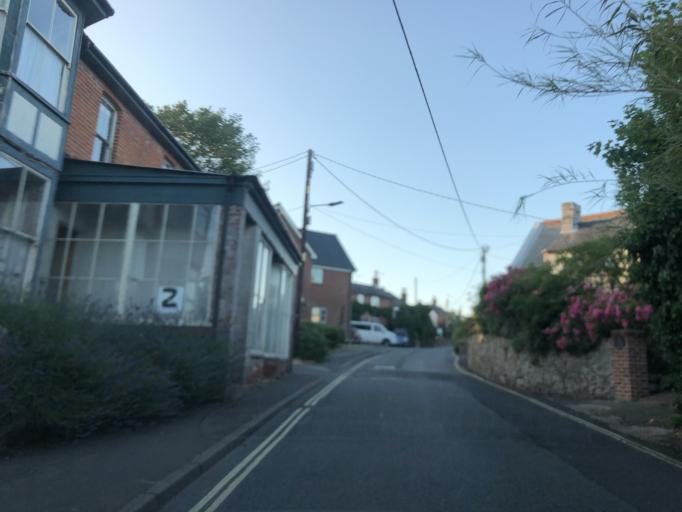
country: GB
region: England
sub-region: Isle of Wight
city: Niton
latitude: 50.5892
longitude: -1.2847
